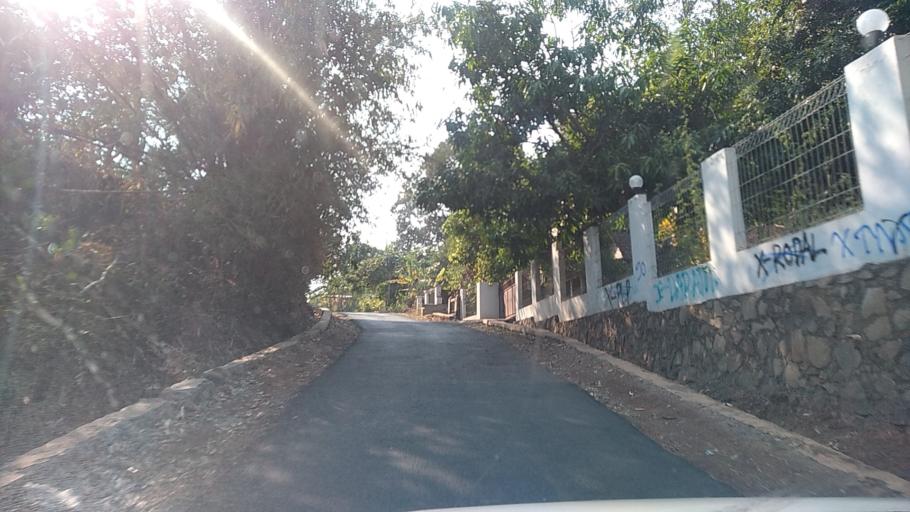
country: ID
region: Central Java
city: Semarang
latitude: -7.0233
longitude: 110.2974
